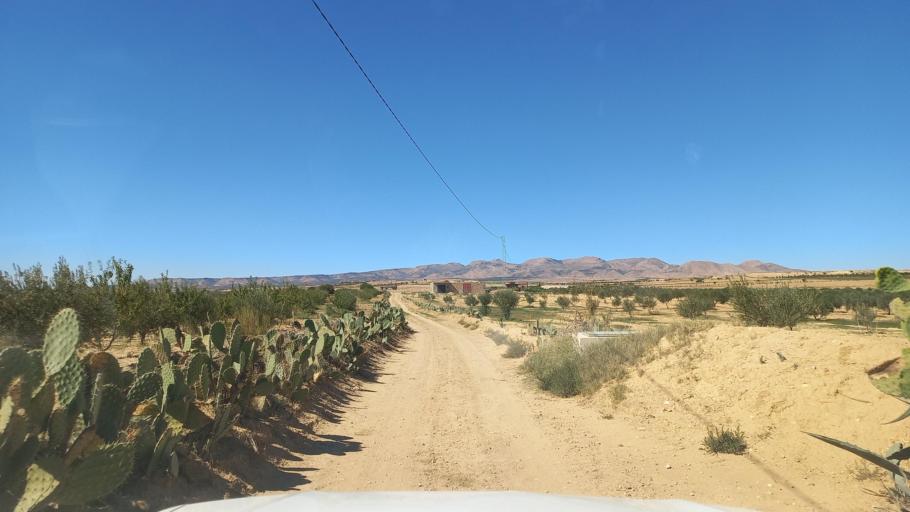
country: TN
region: Al Qasrayn
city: Sbiba
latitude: 35.3657
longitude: 9.0890
